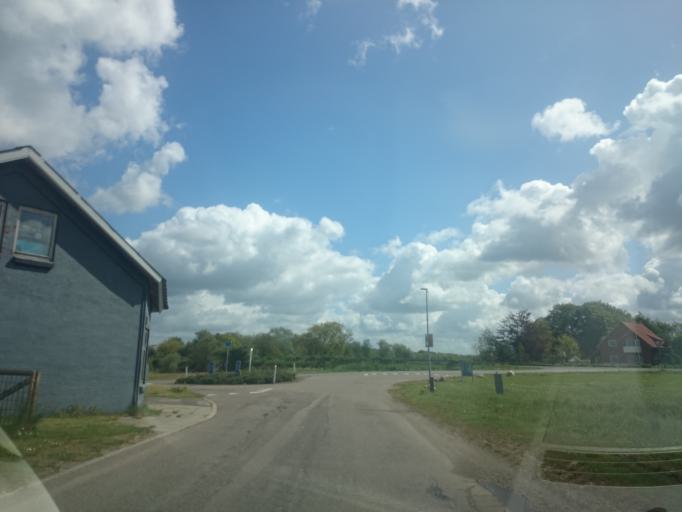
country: DK
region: South Denmark
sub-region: Billund Kommune
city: Grindsted
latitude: 55.6465
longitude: 8.8080
